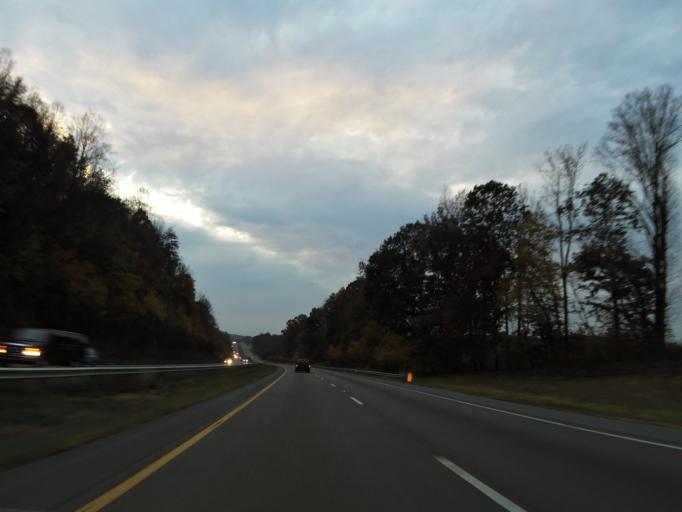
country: US
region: North Carolina
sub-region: Burke County
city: Glen Alpine
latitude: 35.7188
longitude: -81.7387
